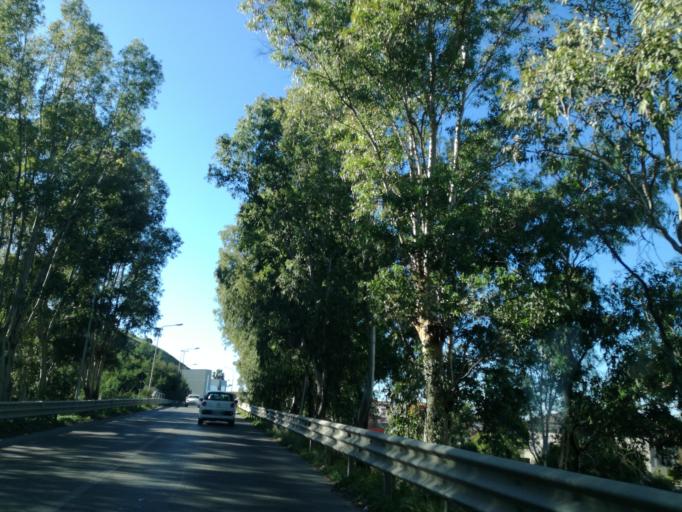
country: IT
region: Sicily
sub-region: Provincia di Caltanissetta
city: Gela
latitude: 37.0805
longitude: 14.2247
